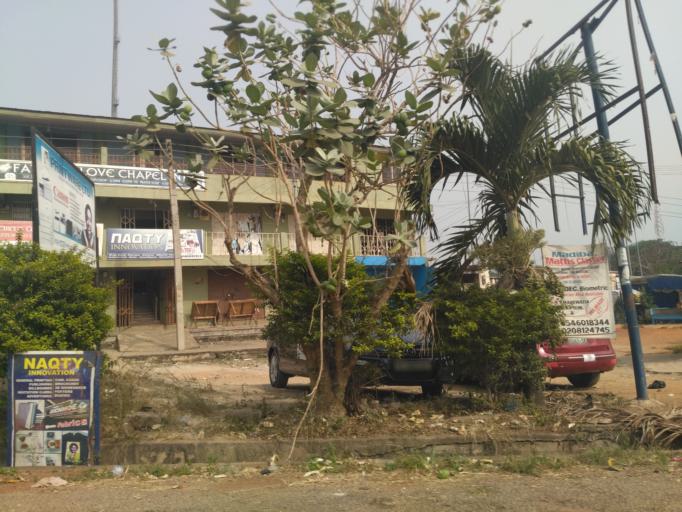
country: GH
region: Ashanti
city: Kumasi
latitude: 6.6816
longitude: -1.6065
